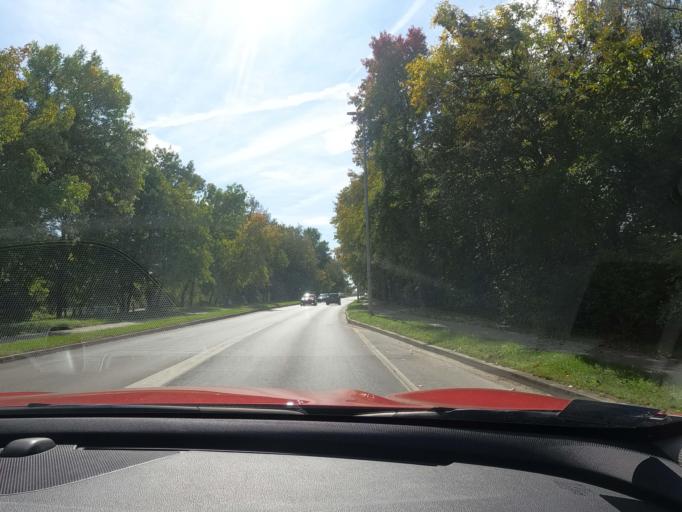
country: HR
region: Sisacko-Moslavacka
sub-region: Grad Sisak
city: Sisak
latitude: 45.4944
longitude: 16.3811
